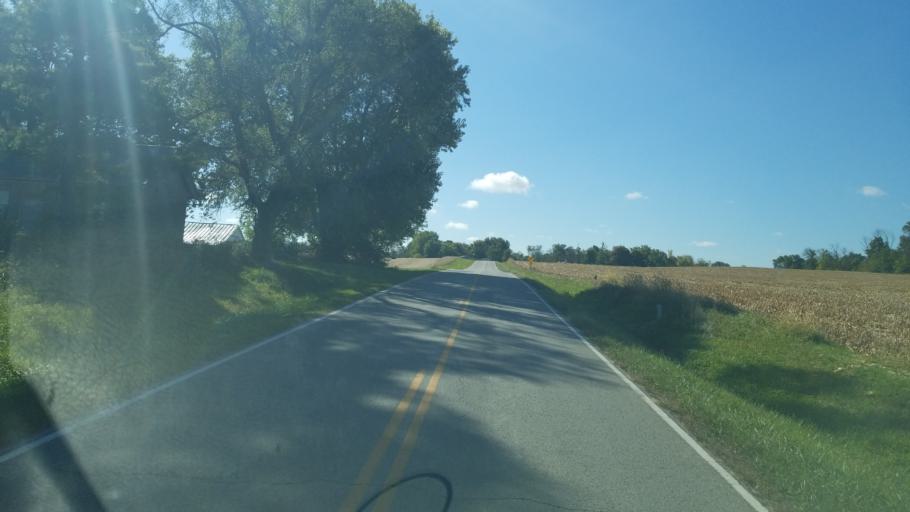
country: US
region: Ohio
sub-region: Highland County
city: Leesburg
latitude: 39.2911
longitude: -83.5800
